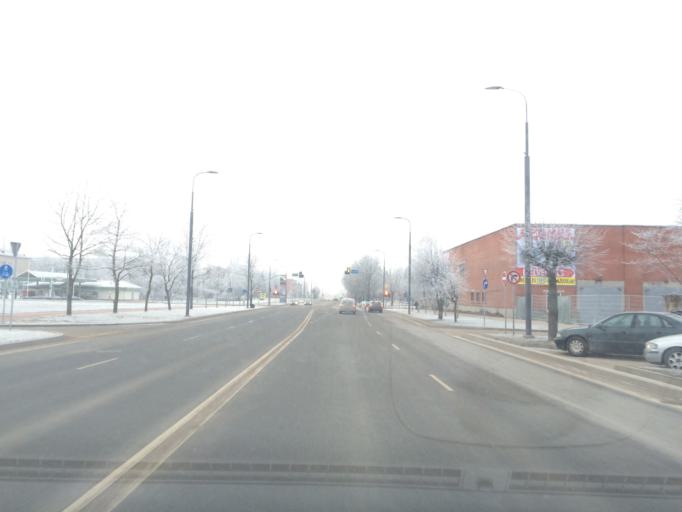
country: LV
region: Rezekne
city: Rezekne
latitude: 56.5279
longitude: 27.3438
